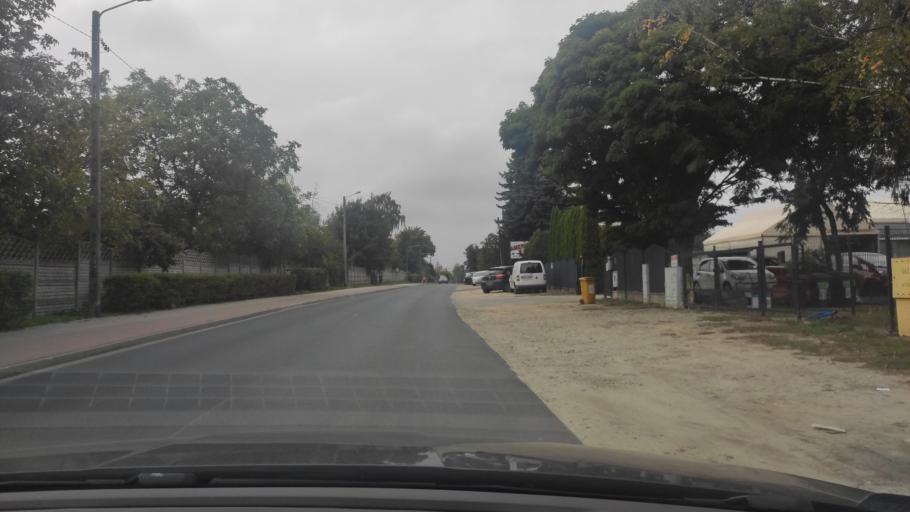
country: PL
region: Greater Poland Voivodeship
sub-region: Powiat poznanski
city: Swarzedz
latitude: 52.4187
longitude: 17.0924
